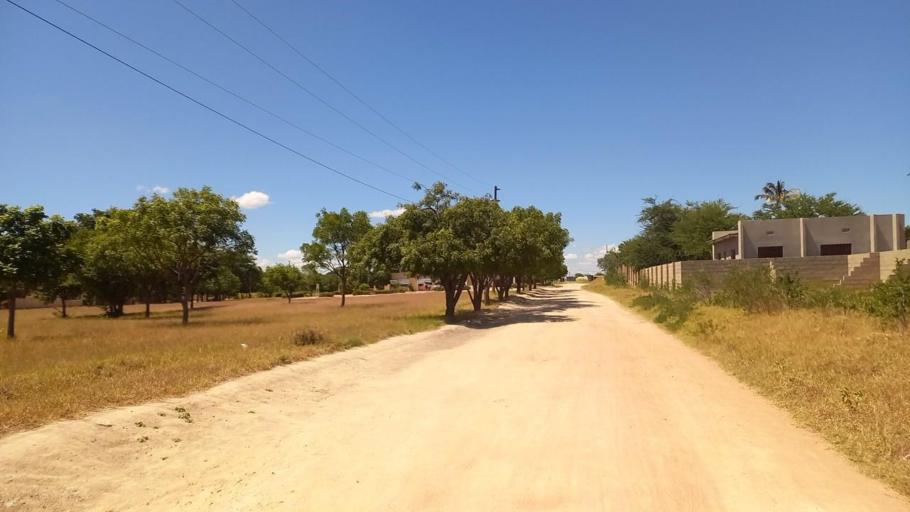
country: TZ
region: Dodoma
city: Dodoma
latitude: -6.1172
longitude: 35.7427
